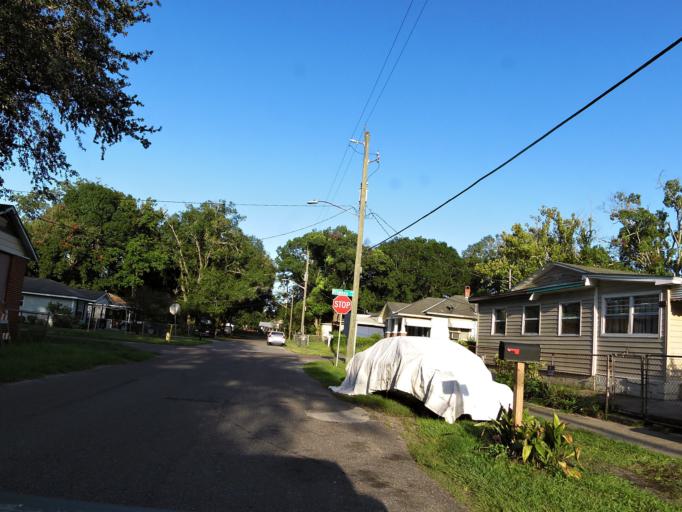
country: US
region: Florida
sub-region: Duval County
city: Jacksonville
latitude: 30.3417
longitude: -81.6903
